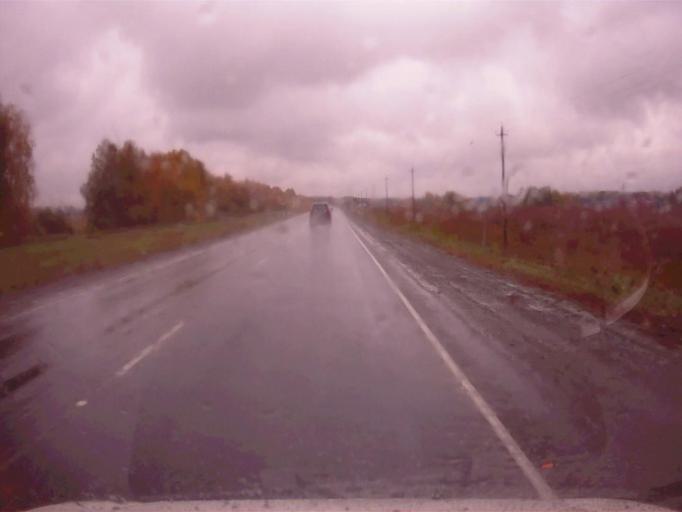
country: RU
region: Chelyabinsk
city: Argayash
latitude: 55.4044
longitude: 61.0636
